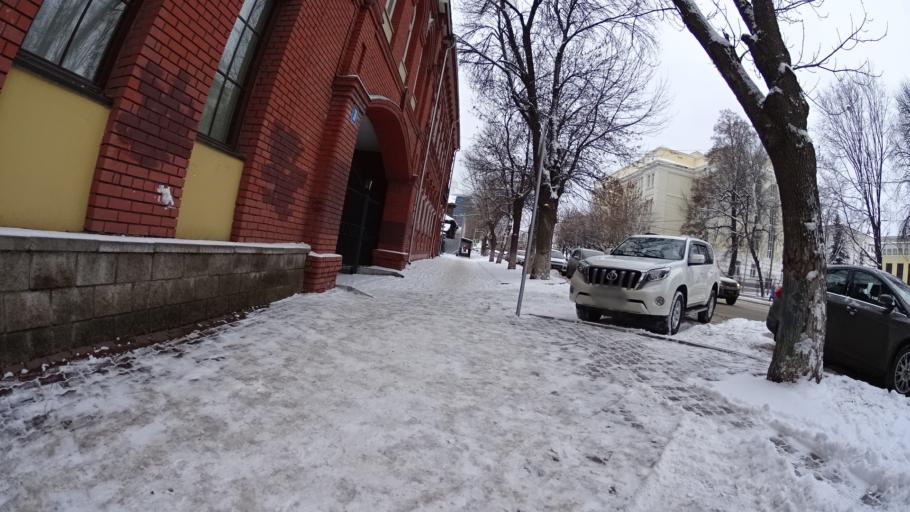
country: RU
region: Bashkortostan
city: Ufa
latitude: 54.7245
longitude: 55.9372
